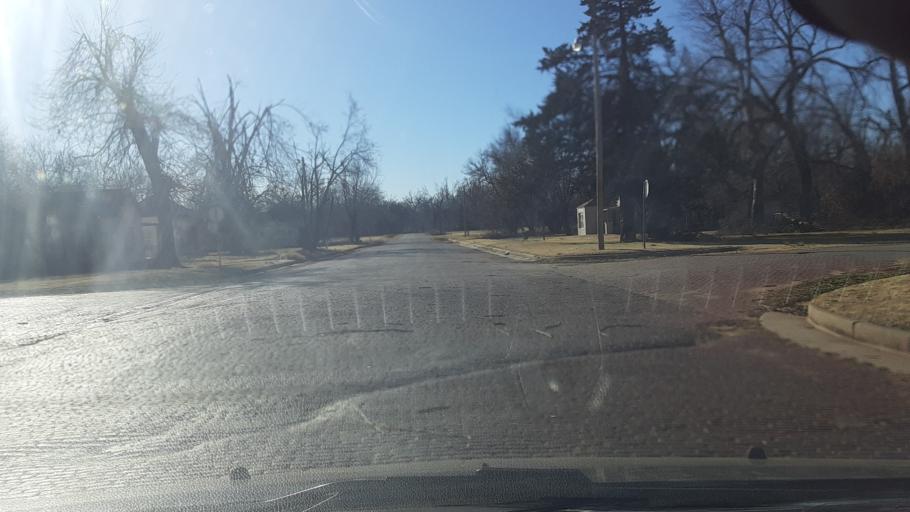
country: US
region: Oklahoma
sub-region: Logan County
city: Guthrie
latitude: 35.8740
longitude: -97.4276
